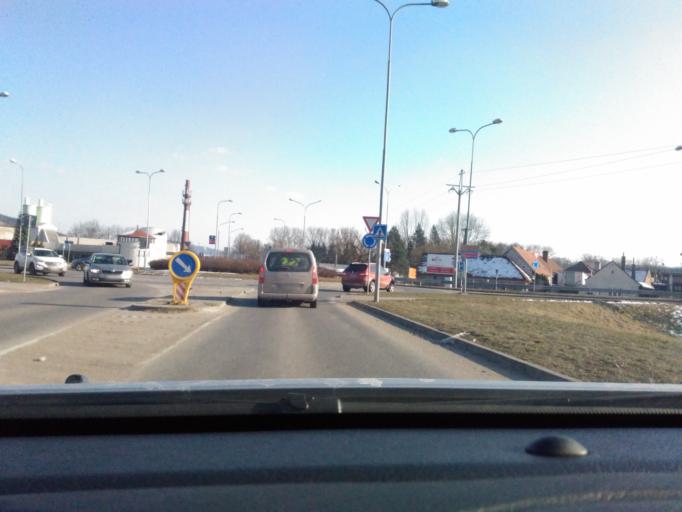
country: CZ
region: South Moravian
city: Tisnov
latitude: 49.3417
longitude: 16.4182
